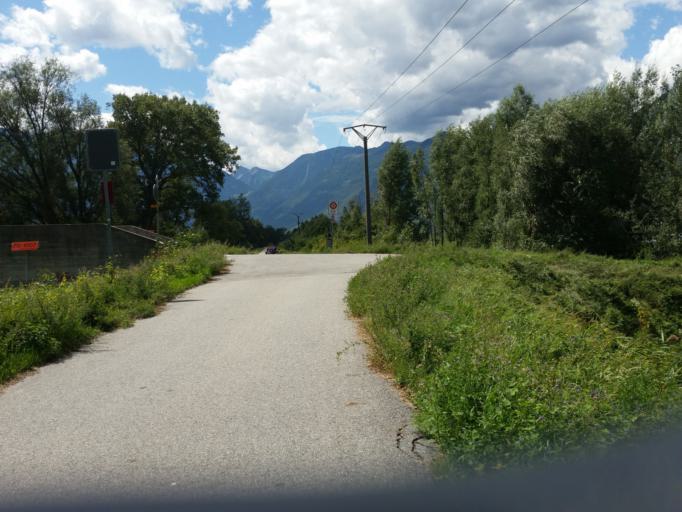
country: CH
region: Valais
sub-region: Martigny District
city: Charrat-les-Chenes
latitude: 46.1429
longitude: 7.1377
